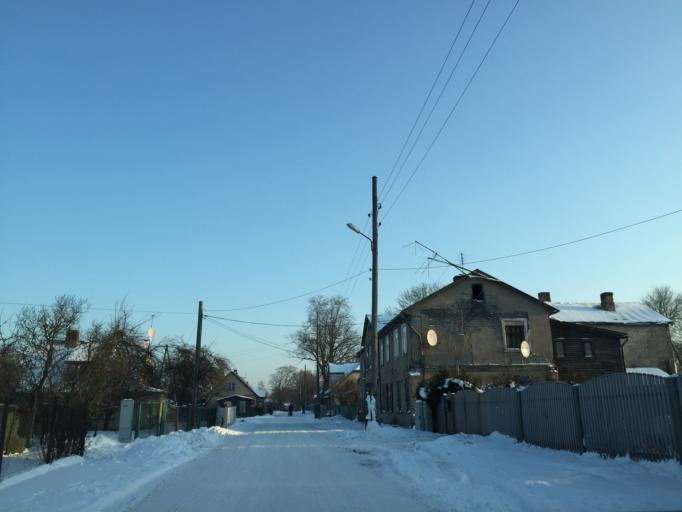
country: LV
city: Tireli
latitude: 56.9431
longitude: 23.6148
